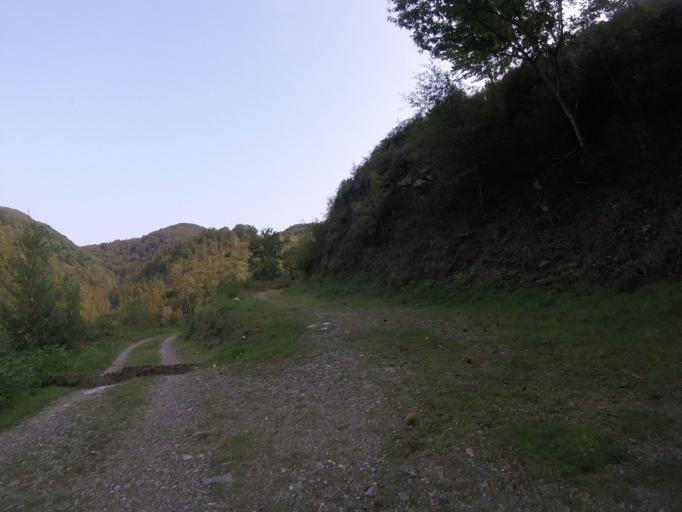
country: ES
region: Navarre
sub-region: Provincia de Navarra
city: Arano
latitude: 43.2542
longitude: -1.8443
